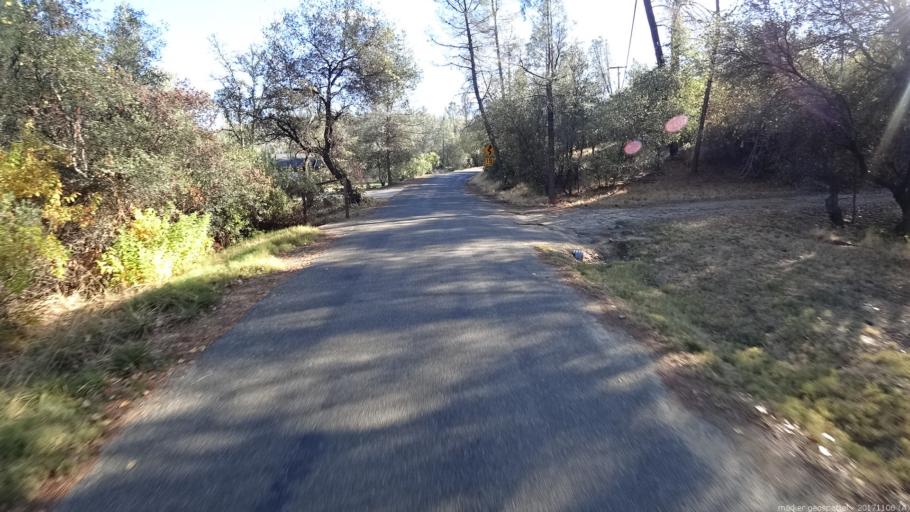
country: US
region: California
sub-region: Shasta County
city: Shasta
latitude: 40.6071
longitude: -122.4900
